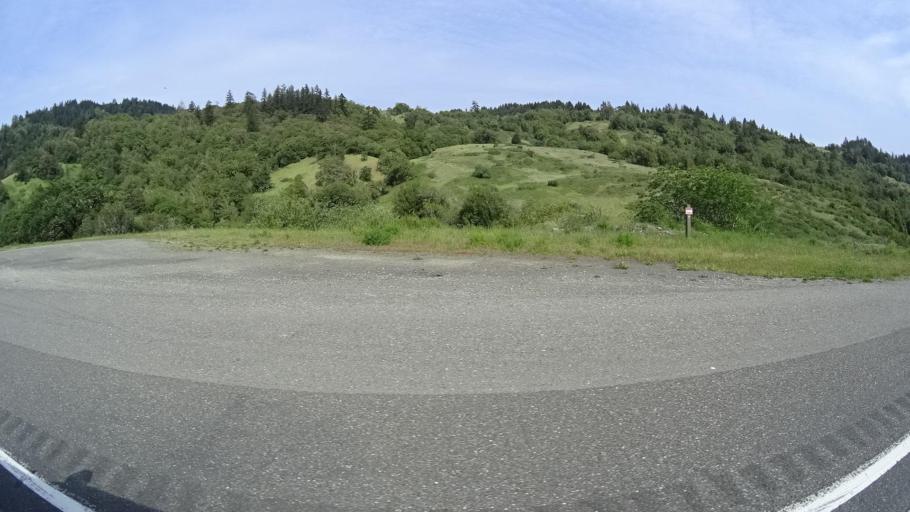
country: US
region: California
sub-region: Humboldt County
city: Redway
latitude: 40.1573
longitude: -123.7937
